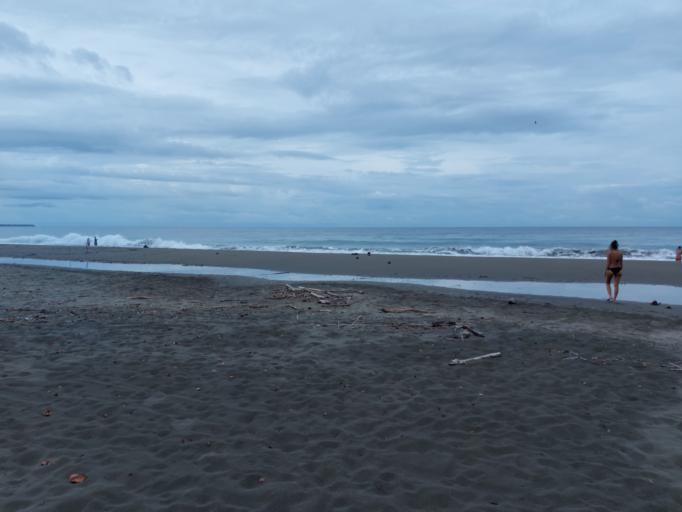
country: PA
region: Bocas del Toro
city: Barranco
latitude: 9.6599
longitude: -82.7746
